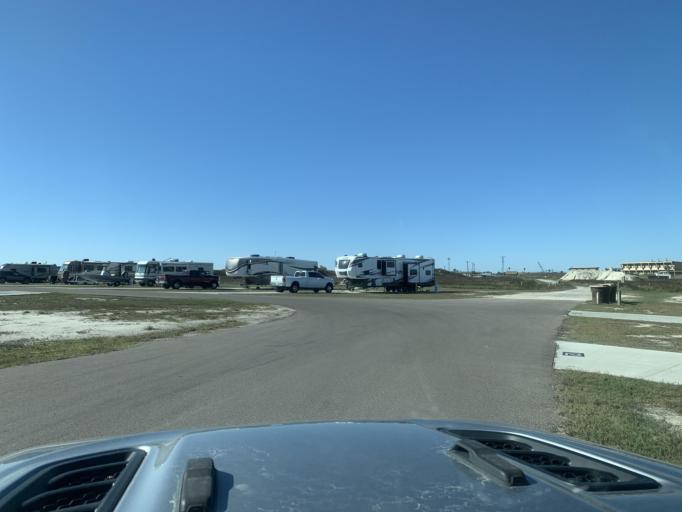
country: US
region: Texas
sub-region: Nueces County
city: Port Aransas
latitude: 27.8331
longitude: -97.0501
